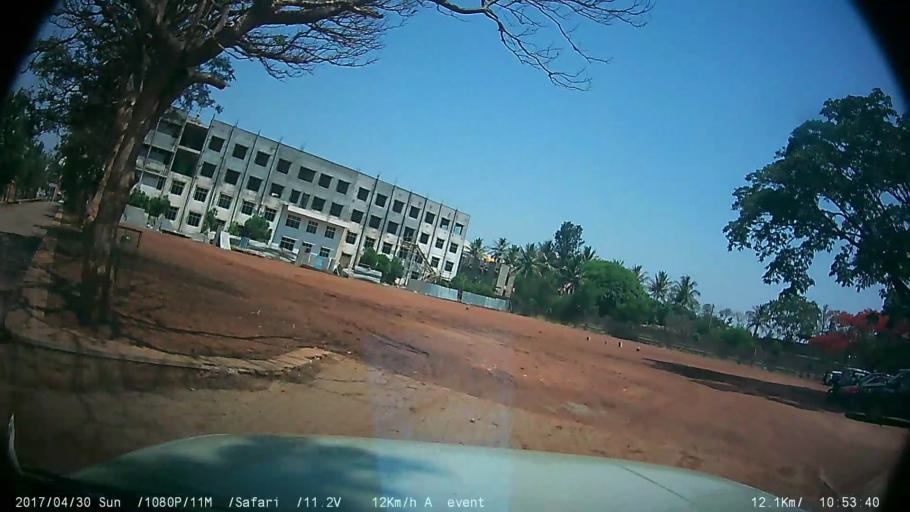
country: IN
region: Karnataka
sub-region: Bangalore Urban
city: Anekal
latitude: 12.8340
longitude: 77.6823
